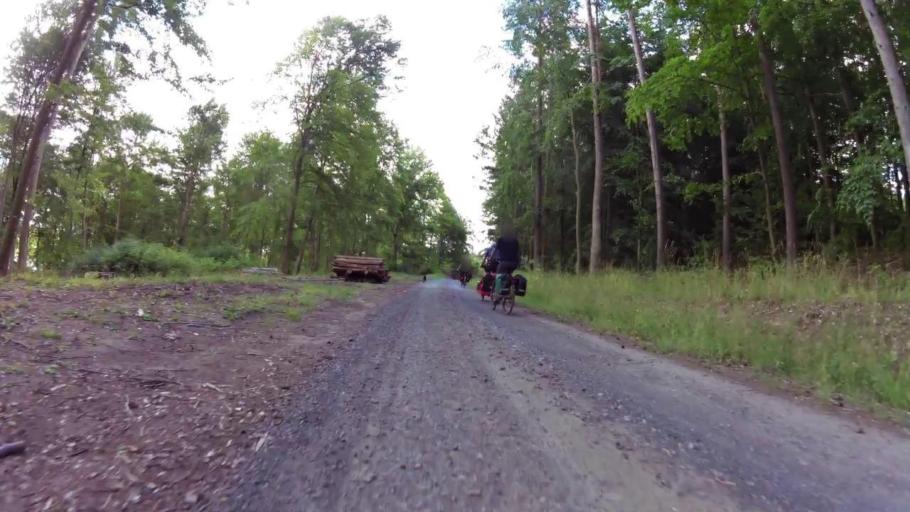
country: PL
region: West Pomeranian Voivodeship
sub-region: Powiat lobeski
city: Lobez
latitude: 53.6882
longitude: 15.5466
